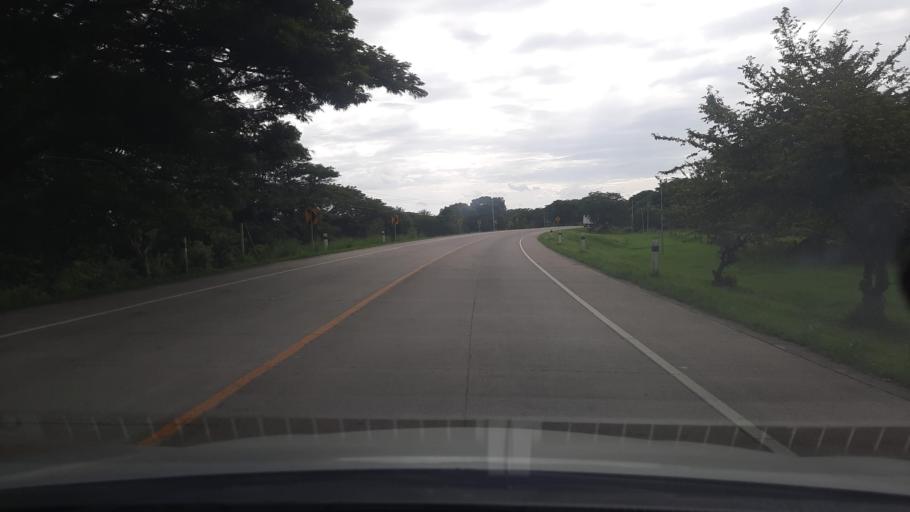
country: NI
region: Chinandega
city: Somotillo
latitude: 12.8598
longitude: -86.8579
